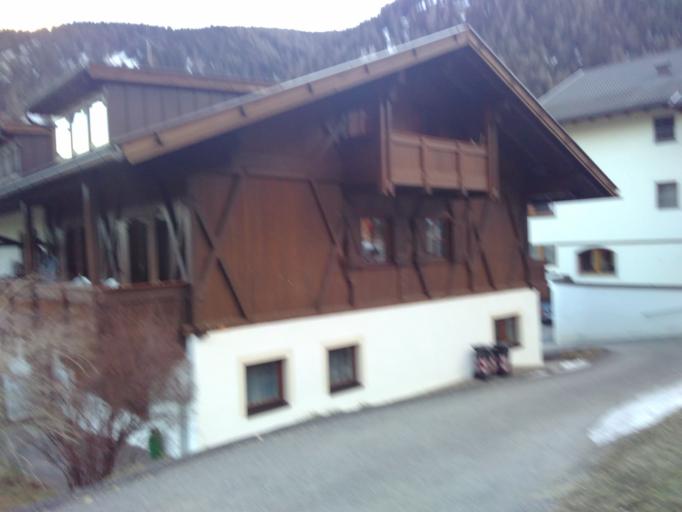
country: IT
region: Trentino-Alto Adige
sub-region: Bolzano
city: Fortezza
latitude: 46.8390
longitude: 11.6282
